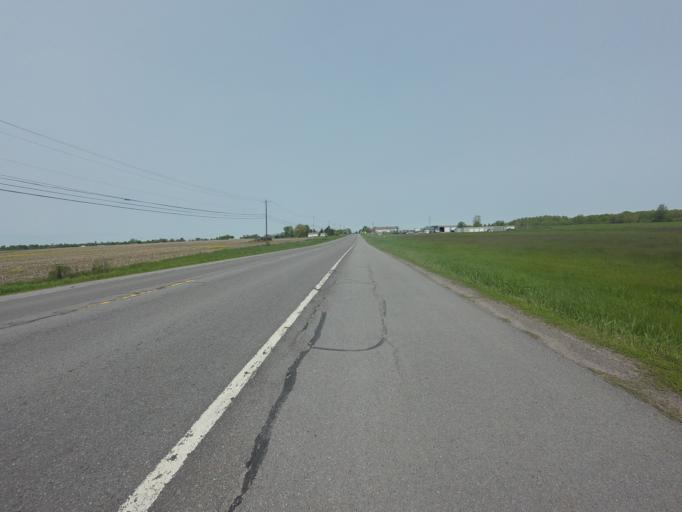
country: US
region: New York
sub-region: Jefferson County
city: Dexter
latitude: 44.0565
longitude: -76.1110
